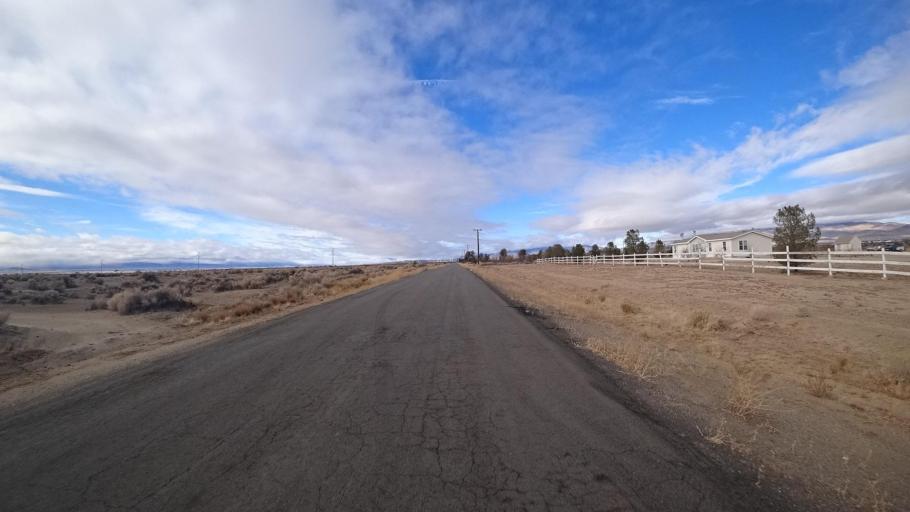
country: US
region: California
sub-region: Kern County
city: Rosamond
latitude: 34.8927
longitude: -118.3044
